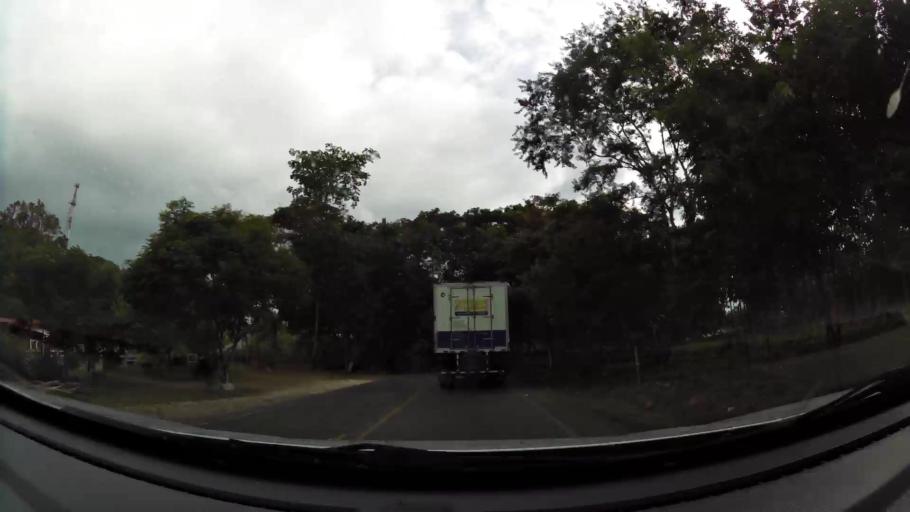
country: CR
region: Guanacaste
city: Juntas
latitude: 10.1529
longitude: -84.9135
